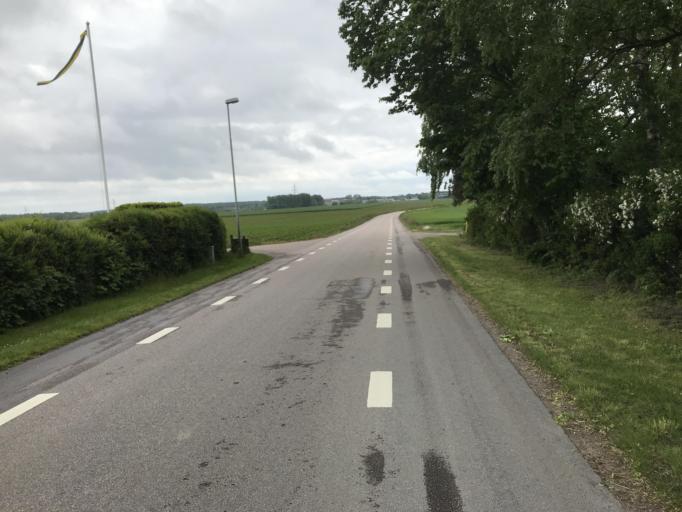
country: SE
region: Skane
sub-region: Landskrona
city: Asmundtorp
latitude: 55.8672
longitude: 12.9263
